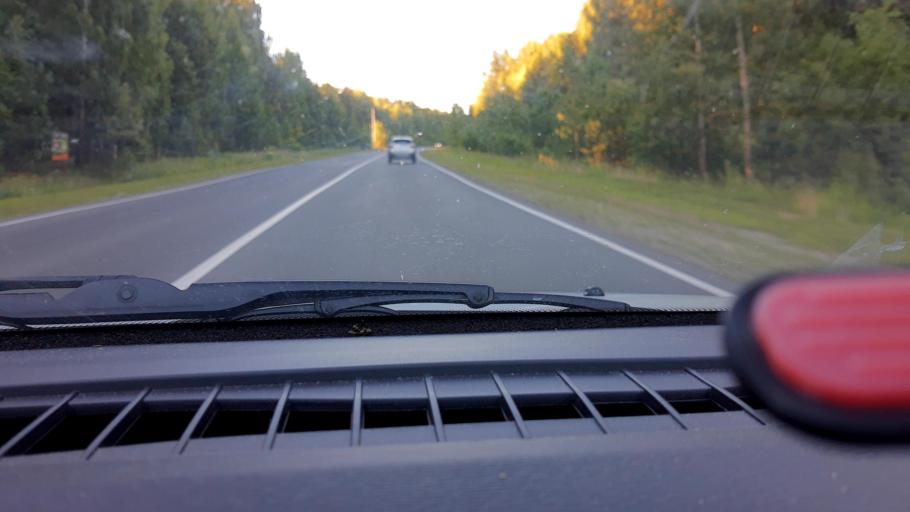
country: RU
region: Nizjnij Novgorod
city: Semenov
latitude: 56.8046
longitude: 44.4621
